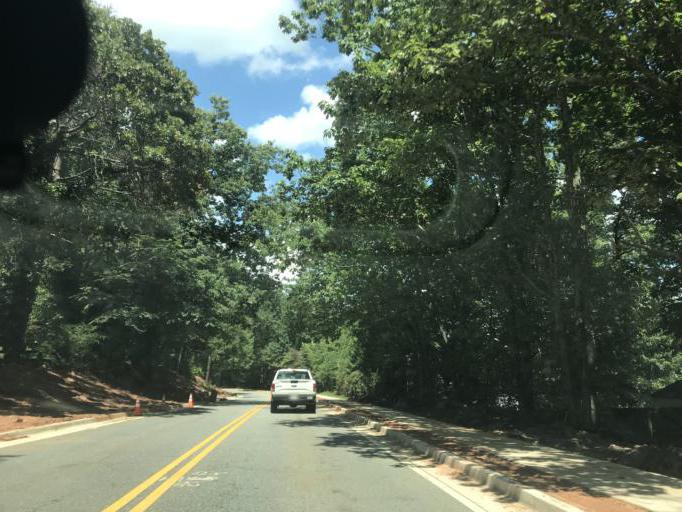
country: US
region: Georgia
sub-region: Forsyth County
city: Cumming
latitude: 34.1765
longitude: -84.1114
